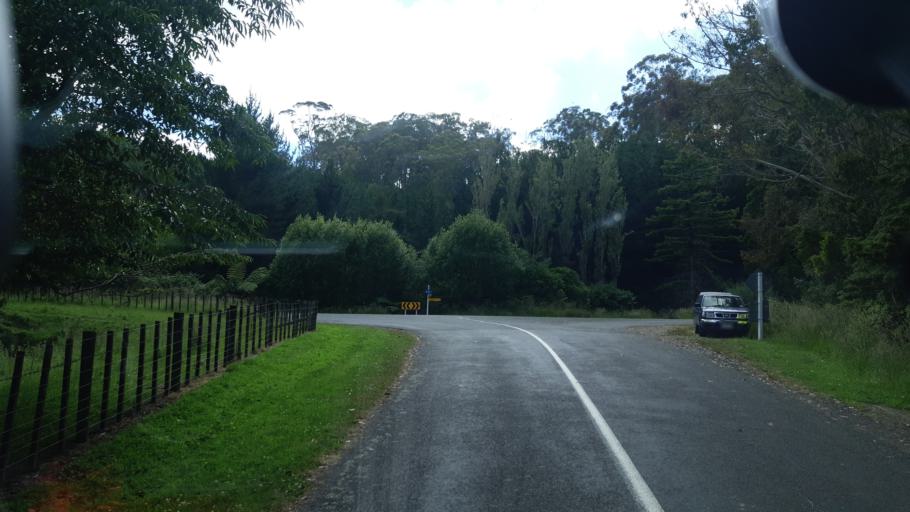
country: NZ
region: Manawatu-Wanganui
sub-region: Rangitikei District
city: Bulls
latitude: -39.9170
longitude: 175.5520
